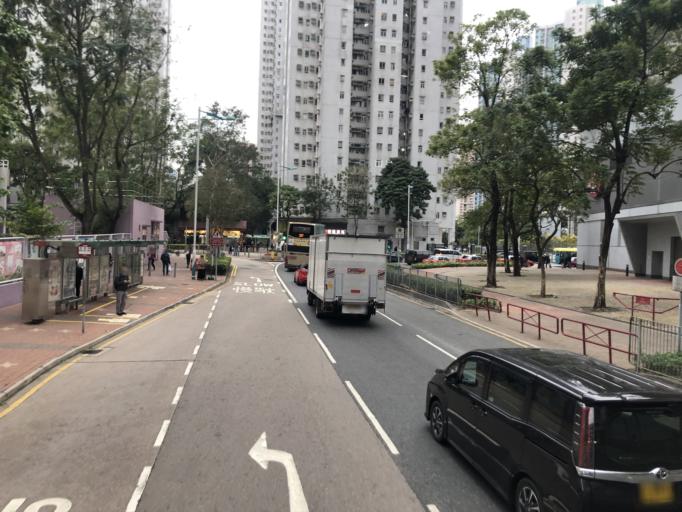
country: HK
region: Sai Kung
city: Sai Kung
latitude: 22.3153
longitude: 114.2640
